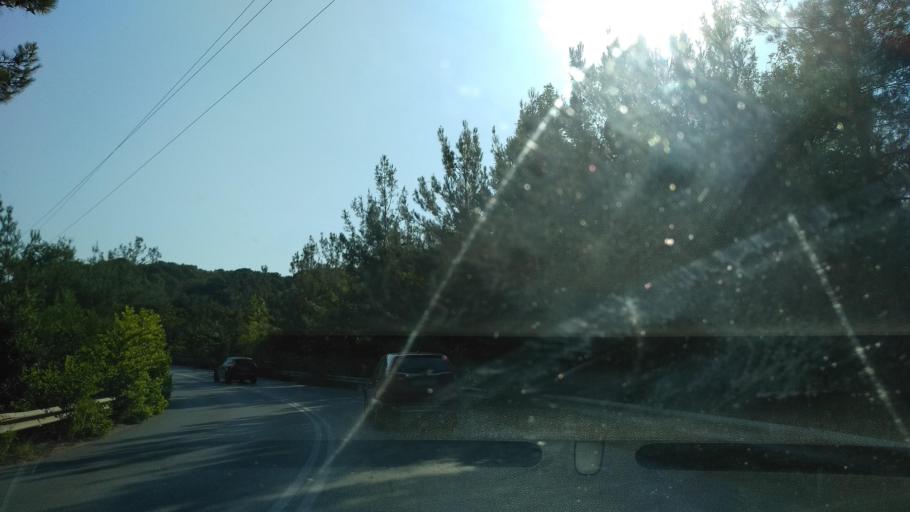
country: GR
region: Central Macedonia
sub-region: Nomos Chalkidikis
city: Stratonion
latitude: 40.5885
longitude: 23.7891
